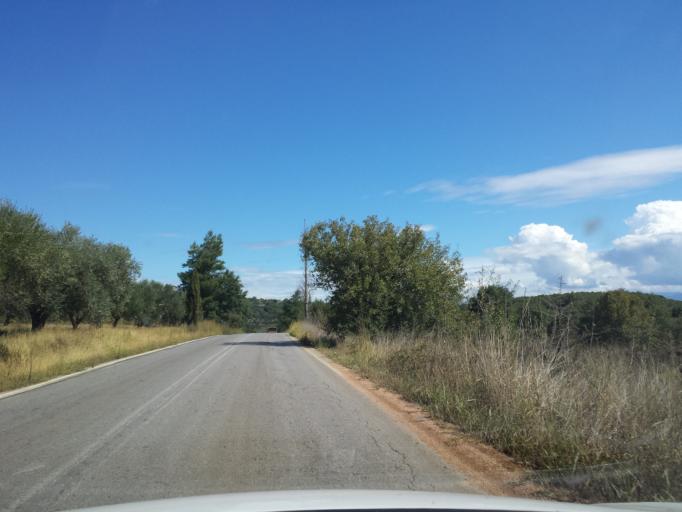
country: GR
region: Peloponnese
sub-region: Nomos Messinias
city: Vlakhopoulon
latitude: 36.9926
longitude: 21.8374
